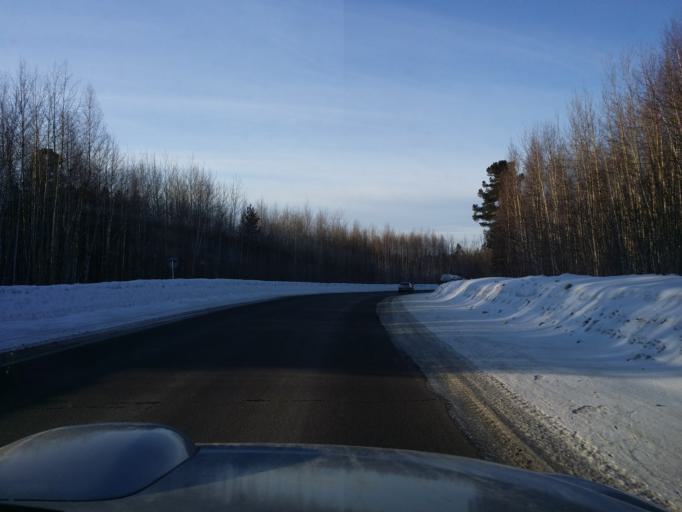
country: RU
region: Khanty-Mansiyskiy Avtonomnyy Okrug
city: Izluchinsk
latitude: 60.9502
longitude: 76.8494
